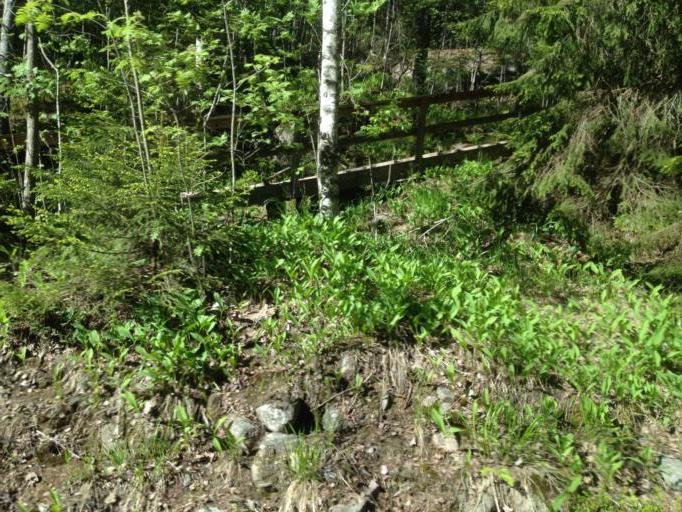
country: FI
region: Uusimaa
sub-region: Helsinki
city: Espoo
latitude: 60.3098
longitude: 24.5173
